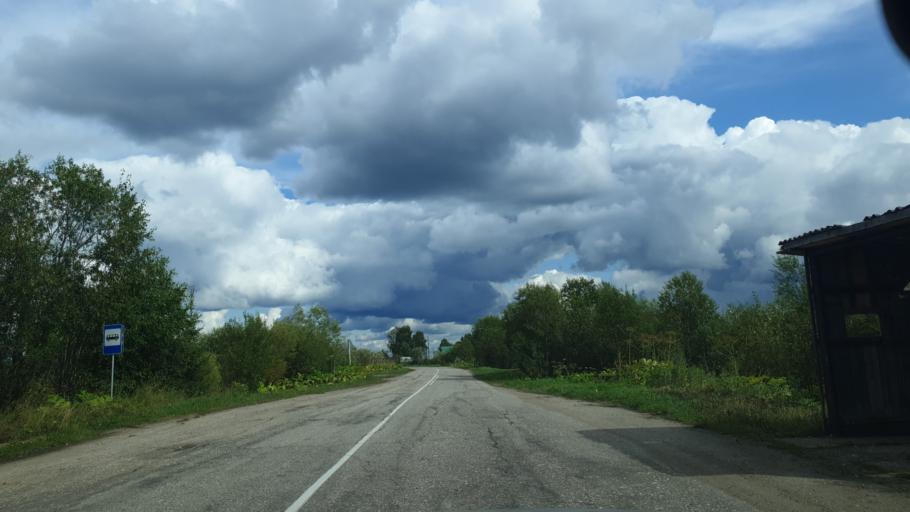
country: RU
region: Komi Republic
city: Aykino
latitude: 61.9526
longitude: 50.1747
